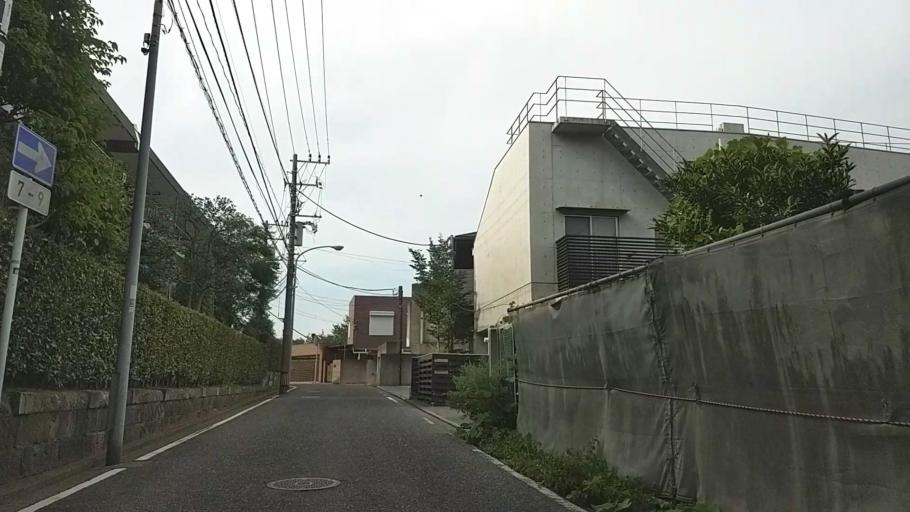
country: JP
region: Kanagawa
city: Yokohama
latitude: 35.4337
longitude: 139.6607
